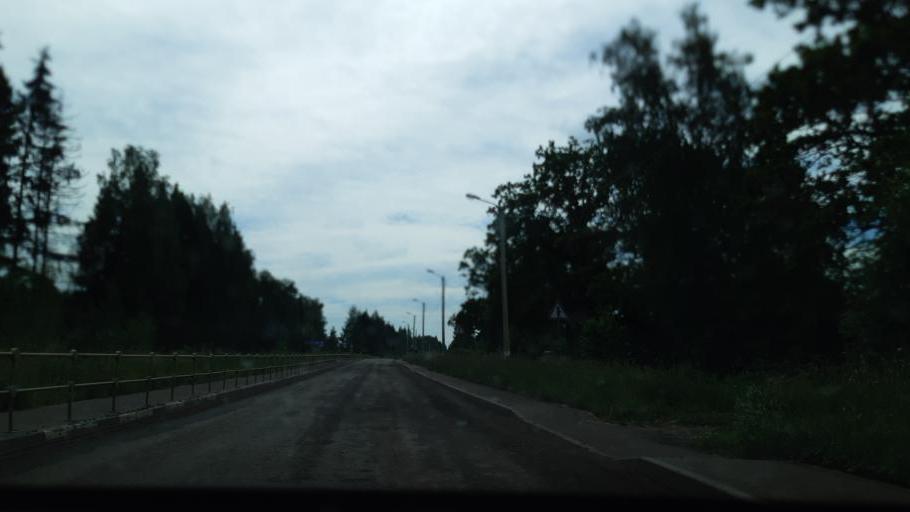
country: RU
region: Moskovskaya
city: Vereya
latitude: 55.3218
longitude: 36.1353
